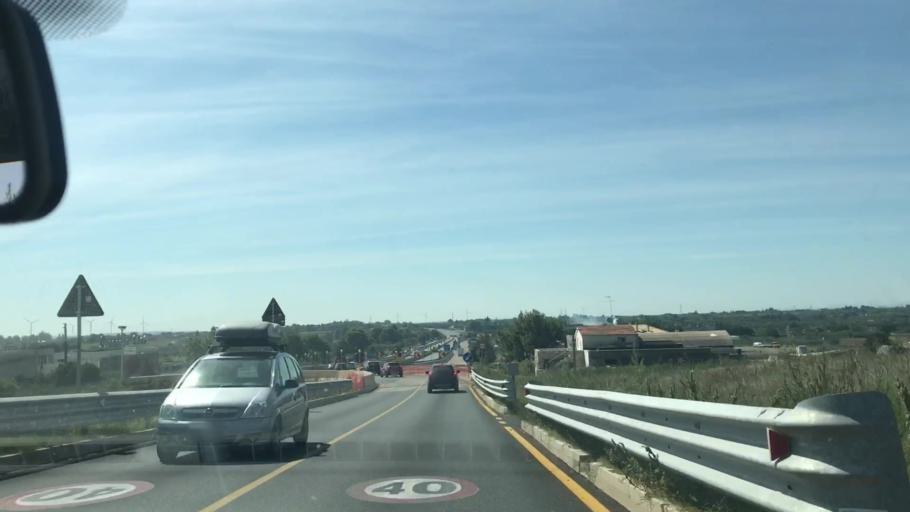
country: IT
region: Apulia
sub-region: Provincia di Bari
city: Altamura
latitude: 40.8074
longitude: 16.5555
